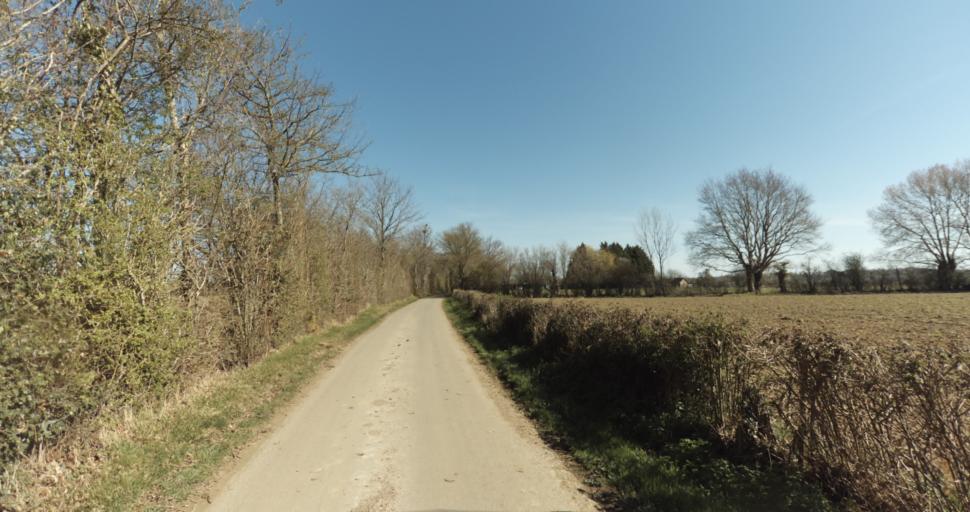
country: FR
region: Lower Normandy
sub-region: Departement du Calvados
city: Livarot
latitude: 48.9917
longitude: 0.0839
